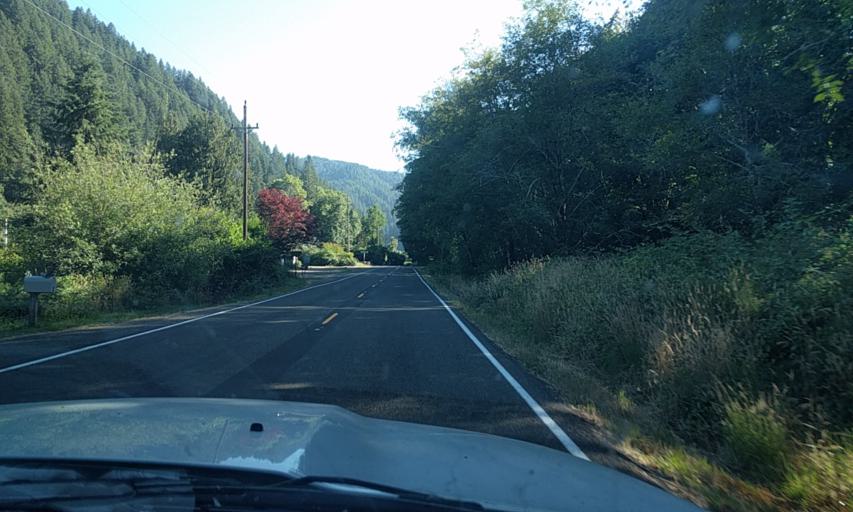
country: US
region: Oregon
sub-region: Lane County
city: Florence
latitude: 44.0680
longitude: -123.8798
